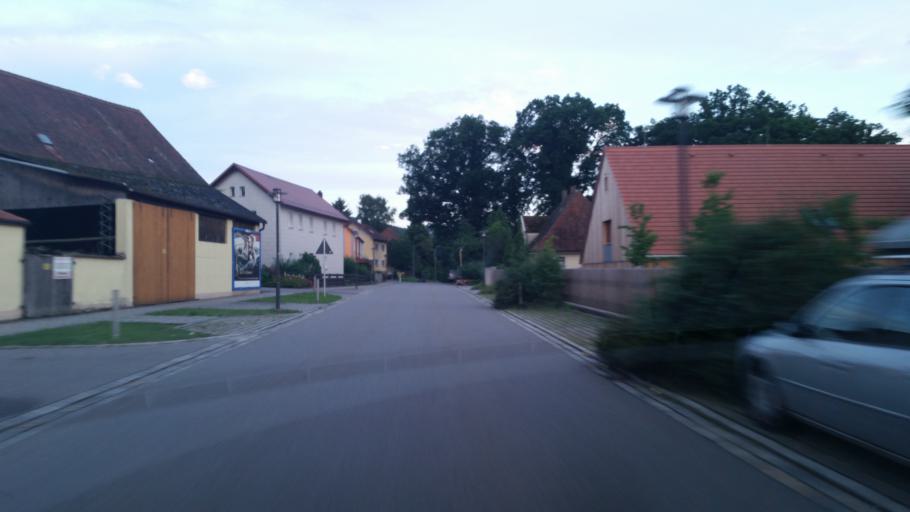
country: DE
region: Bavaria
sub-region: Upper Palatinate
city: Luhe-Wildenau
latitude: 49.5817
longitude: 12.1493
